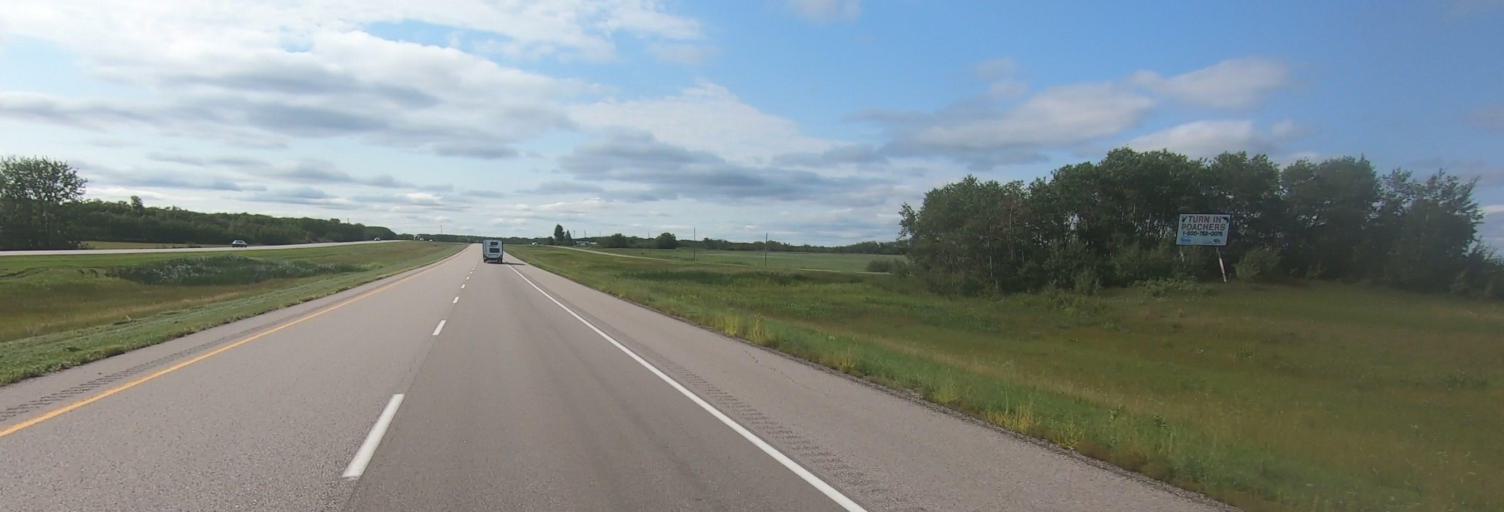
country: CA
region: Manitoba
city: Virden
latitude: 49.7980
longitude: -100.8188
